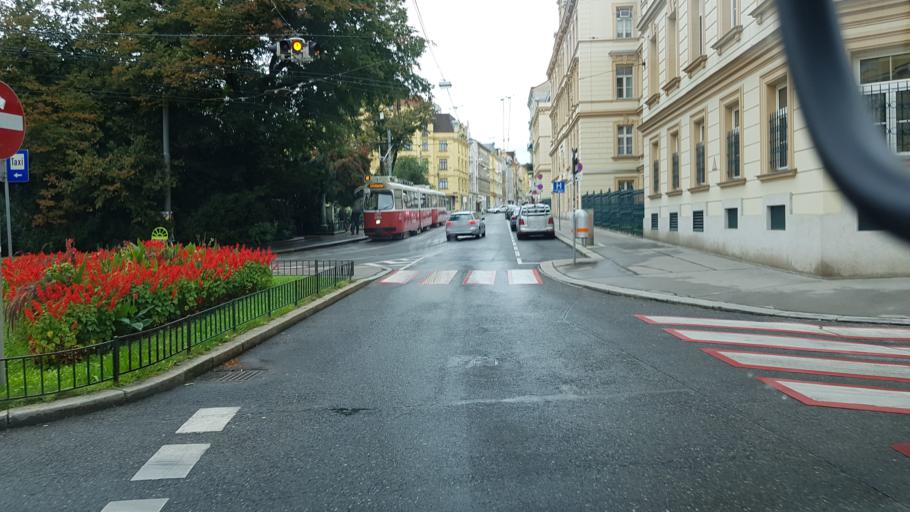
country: AT
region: Vienna
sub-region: Wien Stadt
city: Vienna
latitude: 48.2283
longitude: 16.3369
